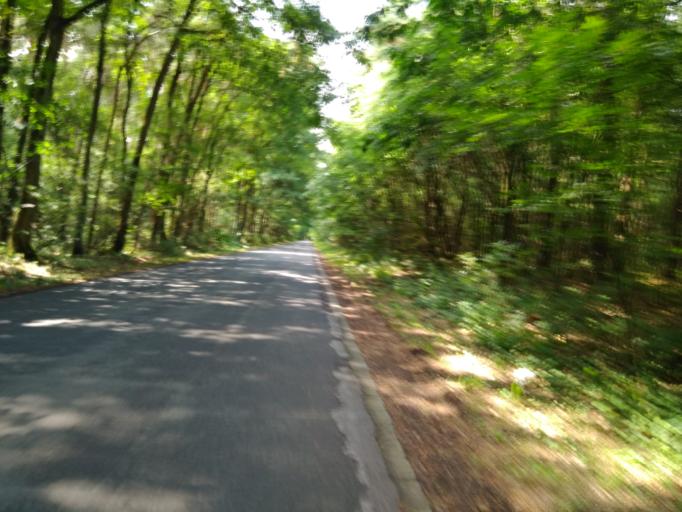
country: DE
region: North Rhine-Westphalia
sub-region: Regierungsbezirk Dusseldorf
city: Schermbeck
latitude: 51.6770
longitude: 6.8997
